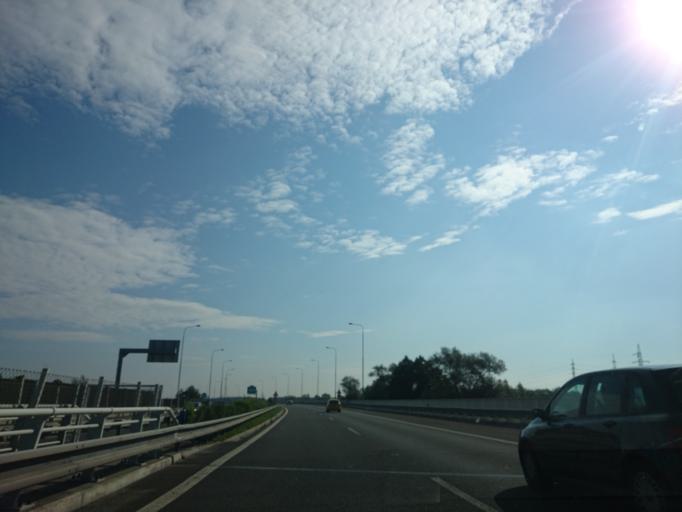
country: CZ
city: Klimkovice
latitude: 49.8032
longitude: 18.1960
